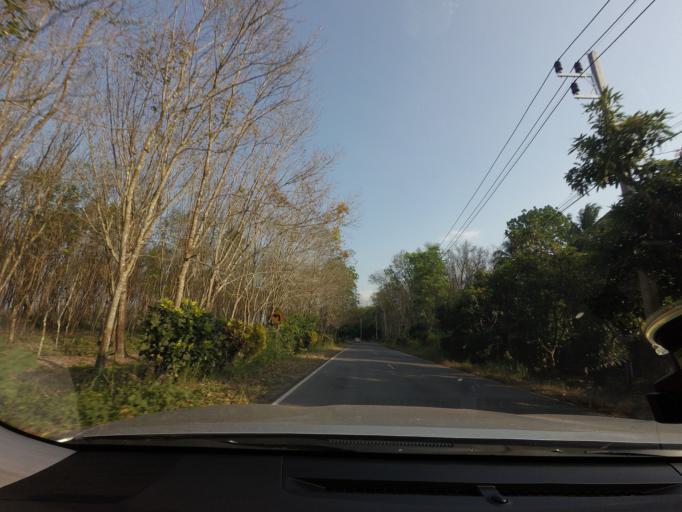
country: TH
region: Surat Thani
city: Phrasaeng
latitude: 8.5669
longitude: 99.2847
